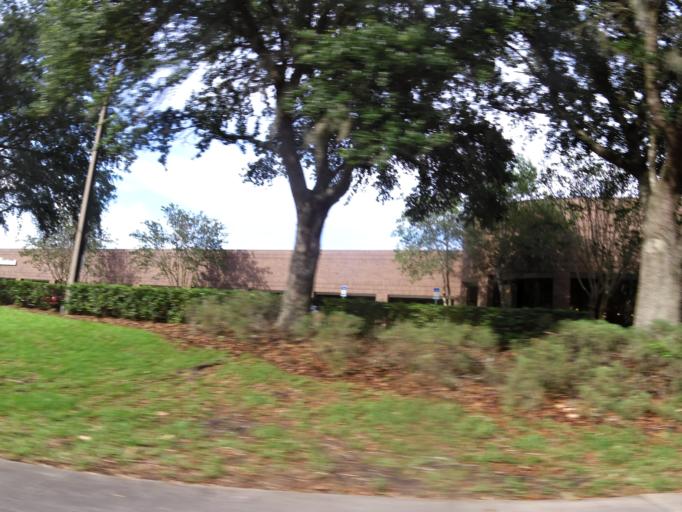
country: US
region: Florida
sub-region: Saint Johns County
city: Fruit Cove
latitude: 30.1774
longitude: -81.5495
